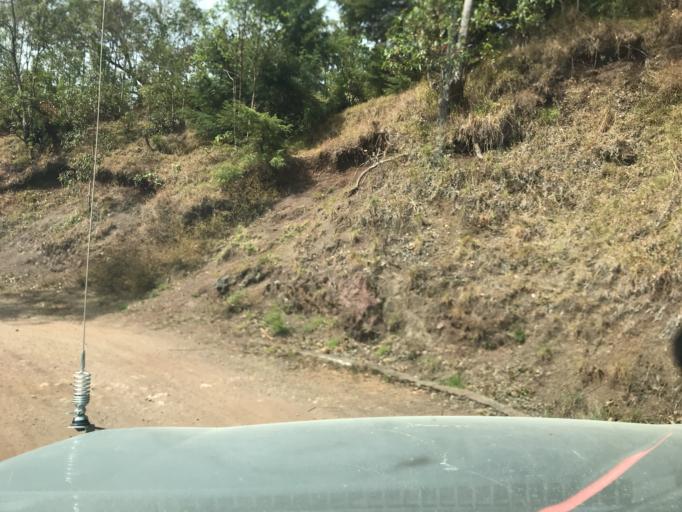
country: TL
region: Ainaro
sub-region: Ainaro
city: Ainaro
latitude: -8.8817
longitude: 125.5390
